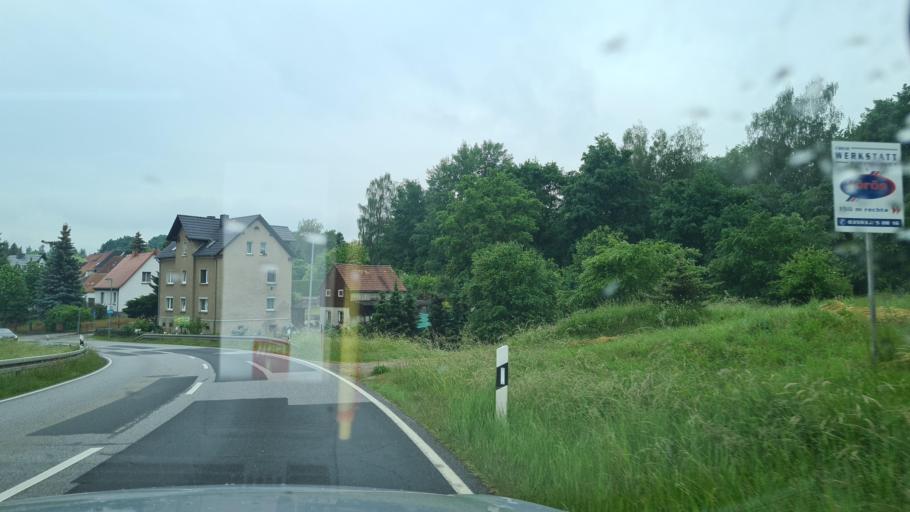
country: DE
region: Saxony
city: Grosspostwitz
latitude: 51.1078
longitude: 14.4452
